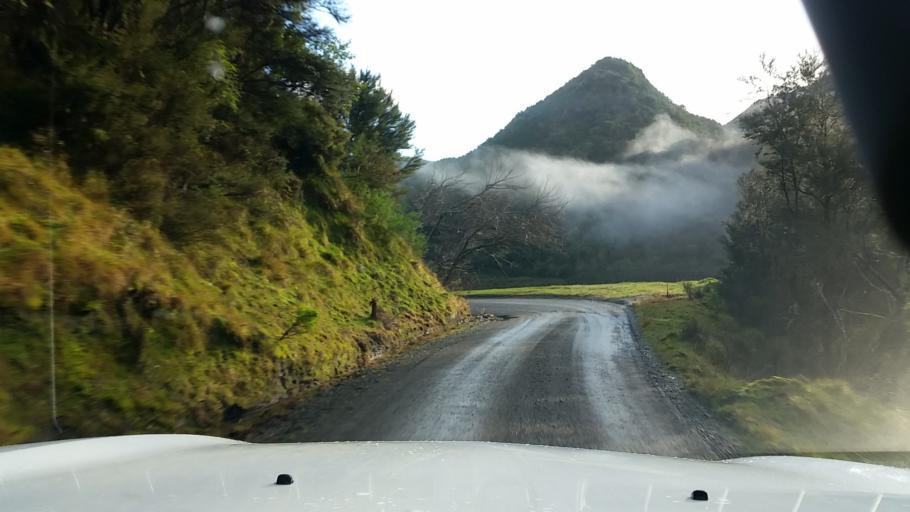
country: NZ
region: Wellington
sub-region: South Wairarapa District
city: Waipawa
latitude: -41.3483
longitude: 175.6757
